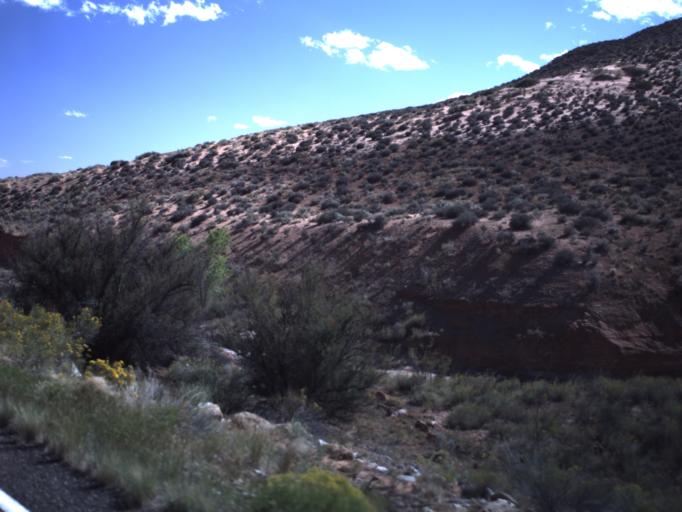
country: US
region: Utah
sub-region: Wayne County
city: Loa
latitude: 38.0547
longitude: -110.5895
